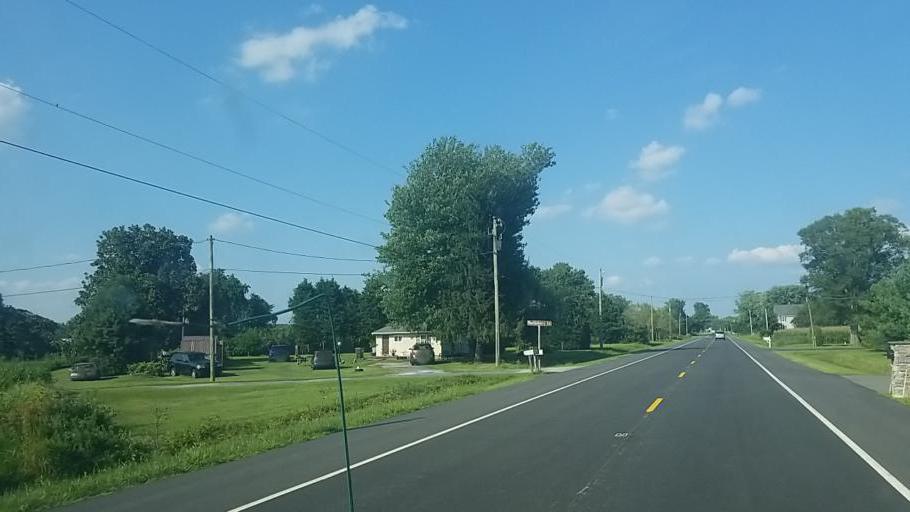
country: US
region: Maryland
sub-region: Worcester County
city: Berlin
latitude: 38.3595
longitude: -75.2103
